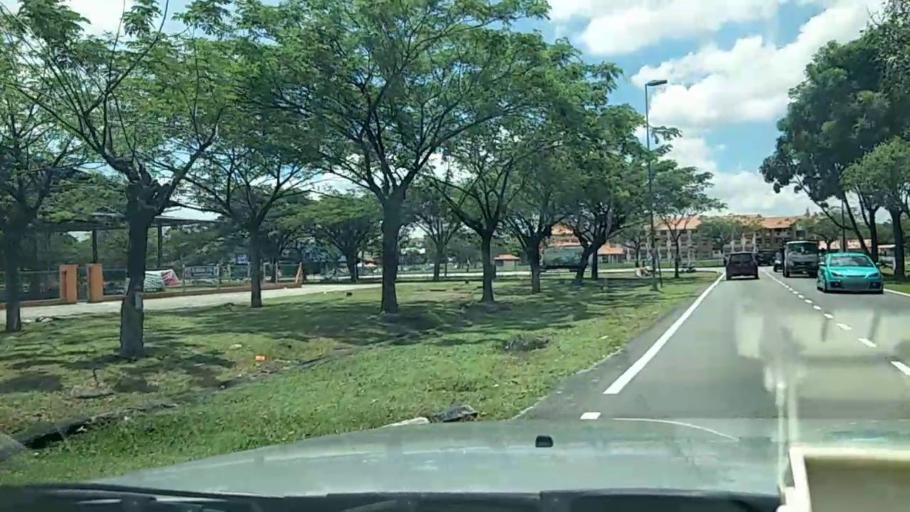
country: MY
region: Putrajaya
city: Putrajaya
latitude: 2.9473
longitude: 101.6201
